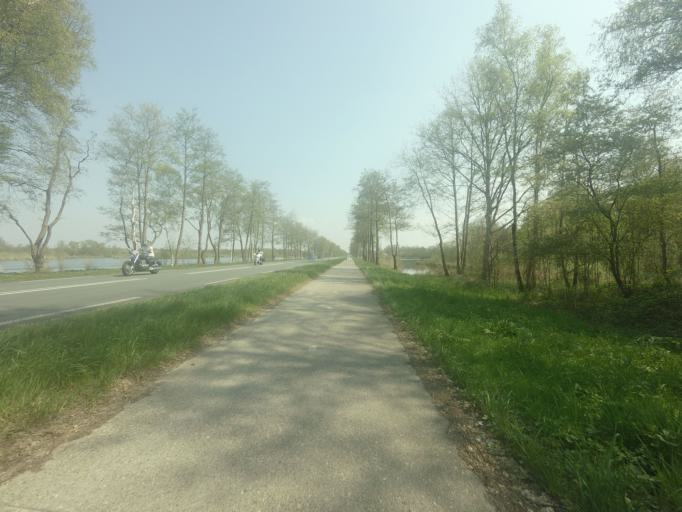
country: NL
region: North Holland
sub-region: Gemeente Wijdemeren
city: Kortenhoef
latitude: 52.2234
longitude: 5.0950
